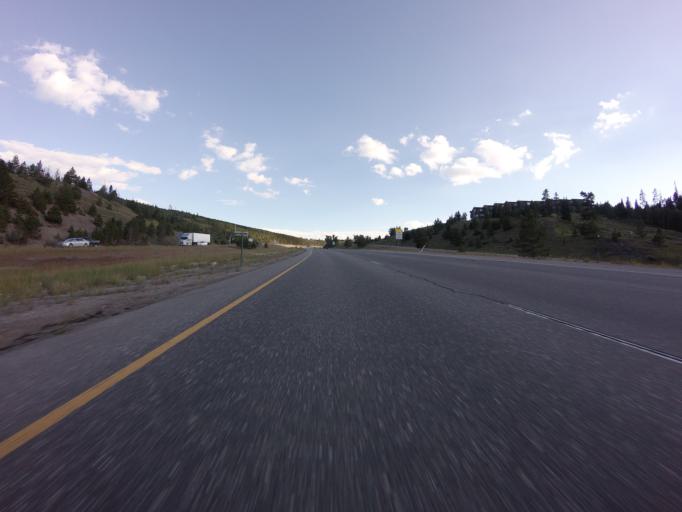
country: US
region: Colorado
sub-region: Summit County
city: Silverthorne
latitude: 39.6211
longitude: -106.0736
